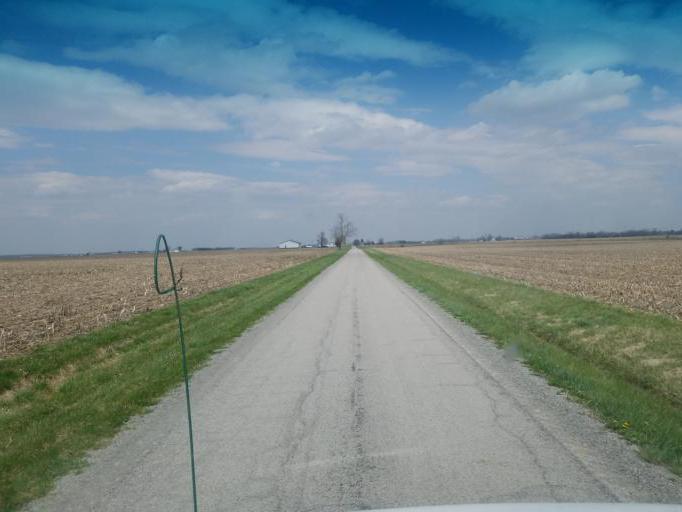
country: US
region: Ohio
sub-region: Wyandot County
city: Upper Sandusky
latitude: 40.7932
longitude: -83.3040
